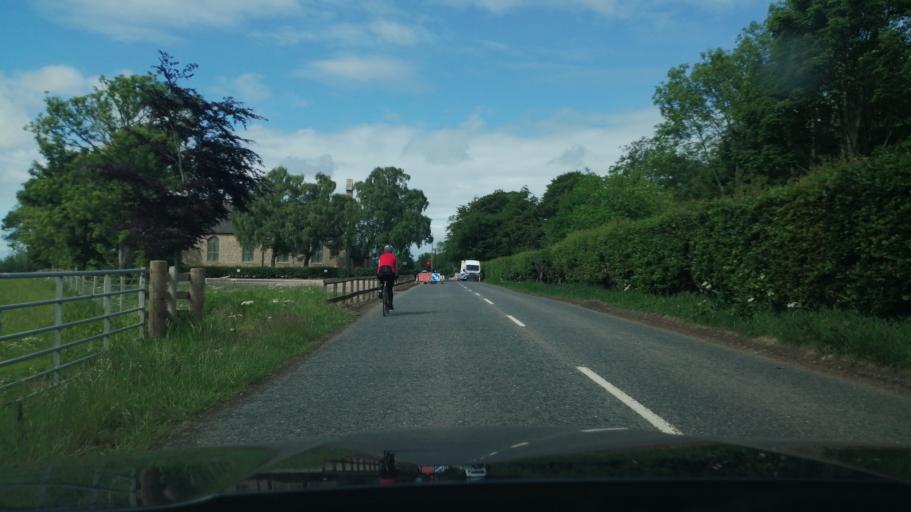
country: GB
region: Scotland
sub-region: Moray
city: Lhanbryd
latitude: 57.6418
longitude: -3.2476
